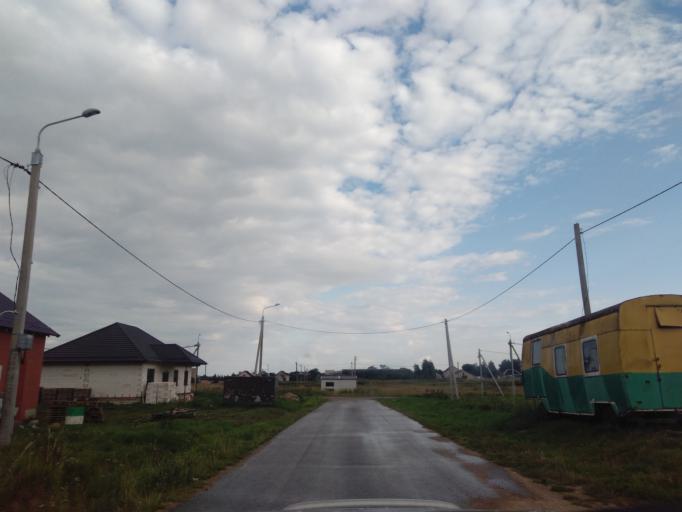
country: BY
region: Minsk
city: Kapyl'
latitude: 53.1638
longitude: 27.0781
